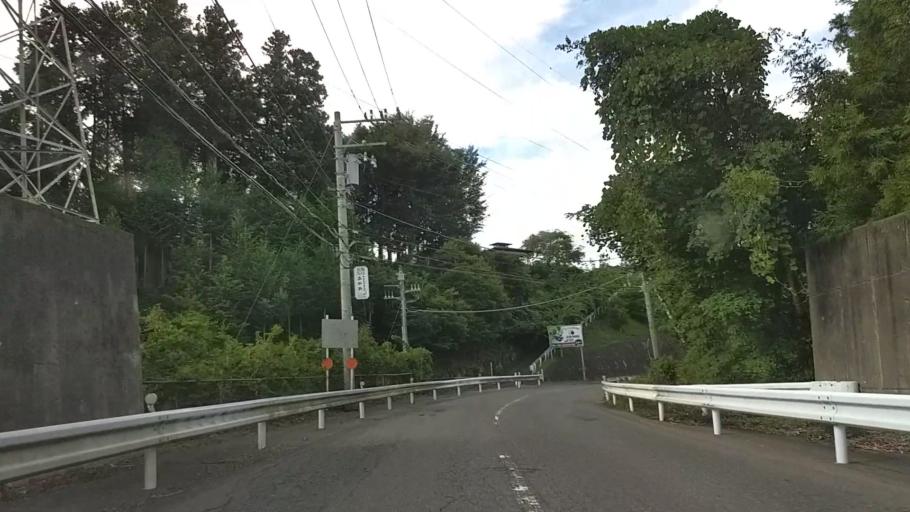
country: JP
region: Yamanashi
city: Uenohara
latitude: 35.5955
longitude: 139.1513
